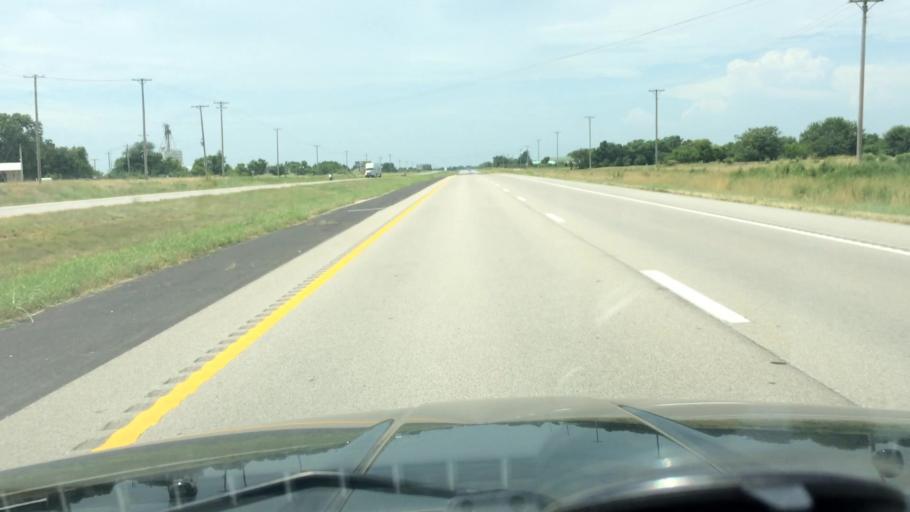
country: US
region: Missouri
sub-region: Polk County
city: Bolivar
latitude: 37.5826
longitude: -93.4114
